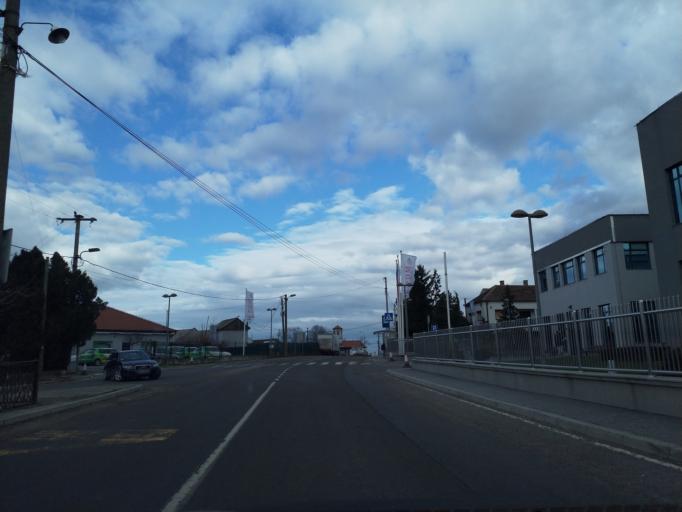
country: RS
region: Central Serbia
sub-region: Belgrade
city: Grocka
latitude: 44.6130
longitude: 20.7240
